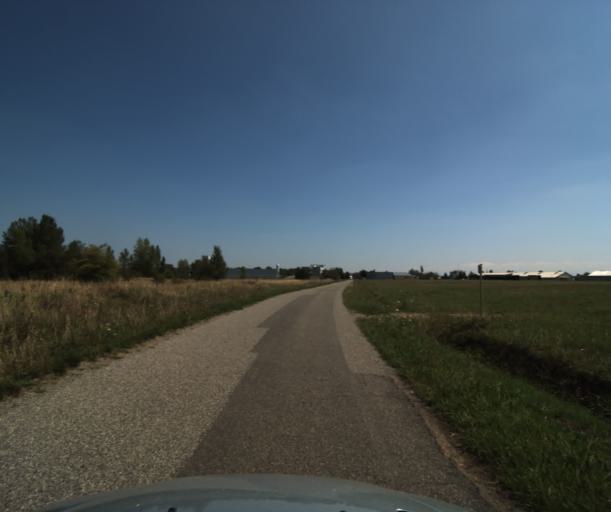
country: FR
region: Midi-Pyrenees
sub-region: Departement de la Haute-Garonne
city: Labastidette
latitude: 43.4525
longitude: 1.2663
